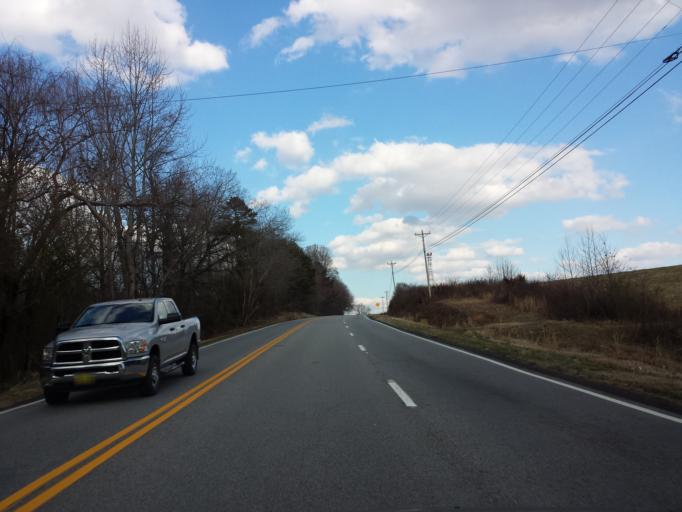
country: US
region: Georgia
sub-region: Lumpkin County
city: Dahlonega
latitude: 34.5279
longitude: -83.8746
